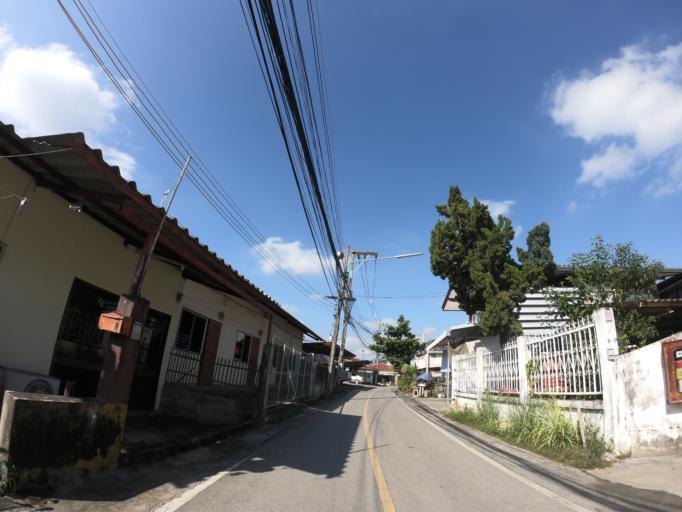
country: TH
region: Chiang Mai
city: Chiang Mai
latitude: 18.7849
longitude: 99.0314
